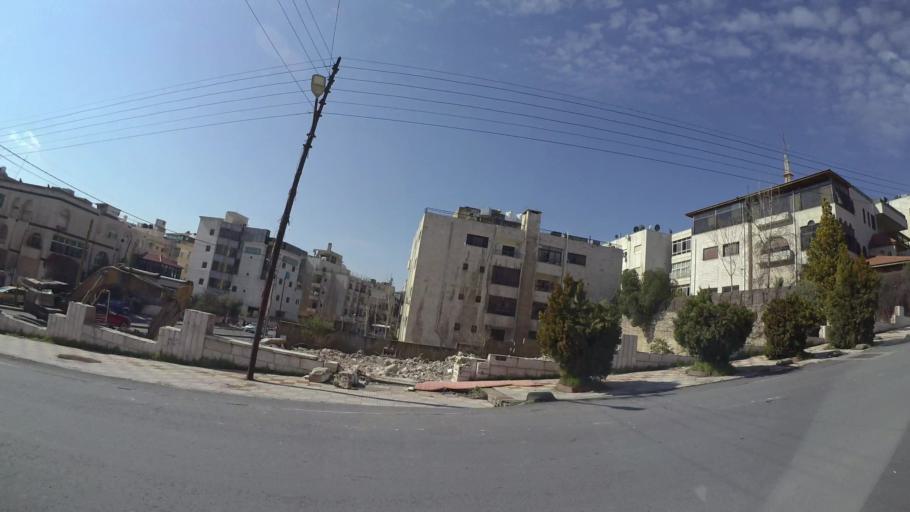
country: JO
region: Amman
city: Al Jubayhah
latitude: 31.9961
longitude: 35.8943
